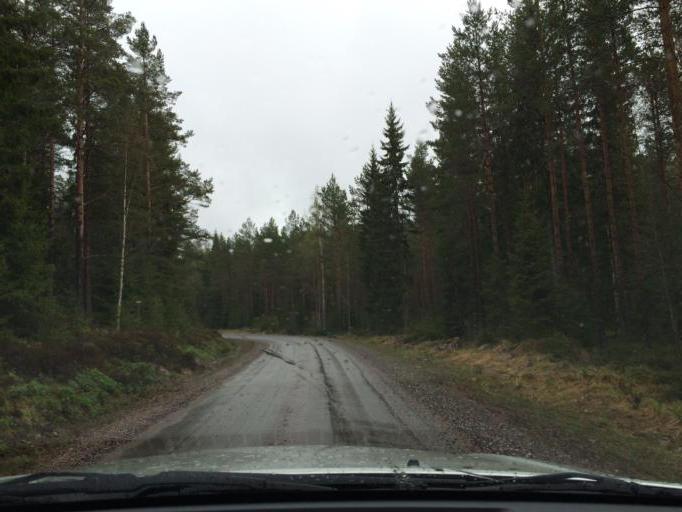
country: SE
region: Dalarna
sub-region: Ludvika Kommun
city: Abborrberget
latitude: 60.0382
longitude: 14.6445
